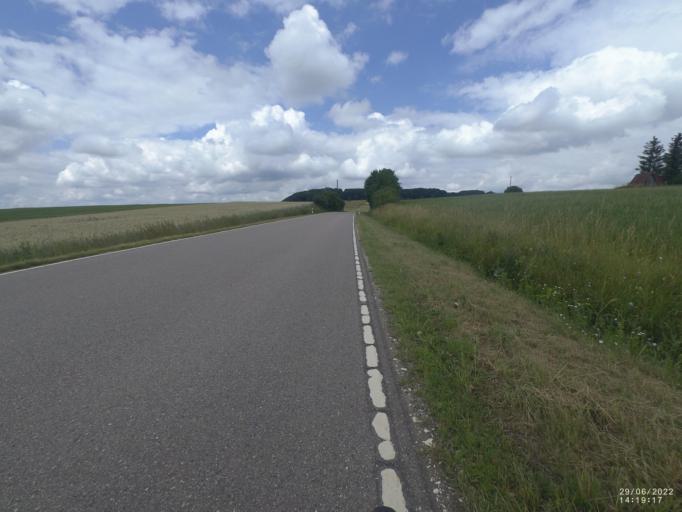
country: DE
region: Baden-Wuerttemberg
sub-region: Regierungsbezirk Stuttgart
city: Gerstetten
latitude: 48.6326
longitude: 10.0154
